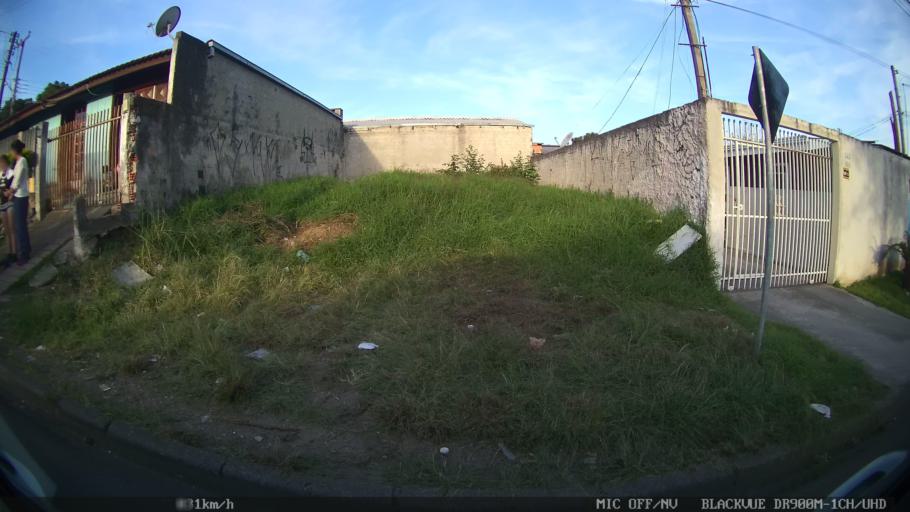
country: BR
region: Parana
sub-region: Pinhais
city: Pinhais
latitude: -25.4509
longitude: -49.1759
